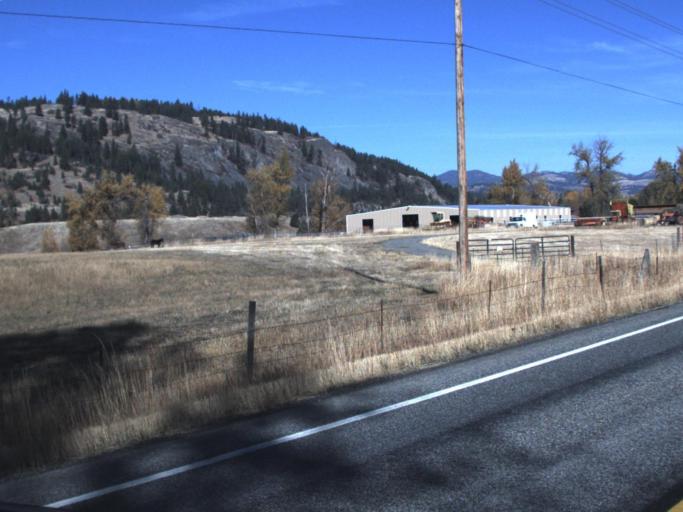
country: US
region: Washington
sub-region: Ferry County
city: Republic
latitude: 48.6755
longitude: -118.6653
